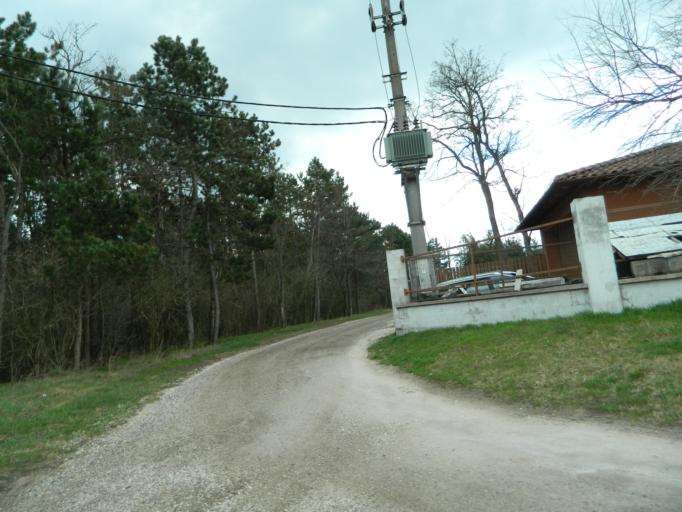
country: HU
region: Fejer
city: Szekesfehervar
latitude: 47.1656
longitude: 18.3799
